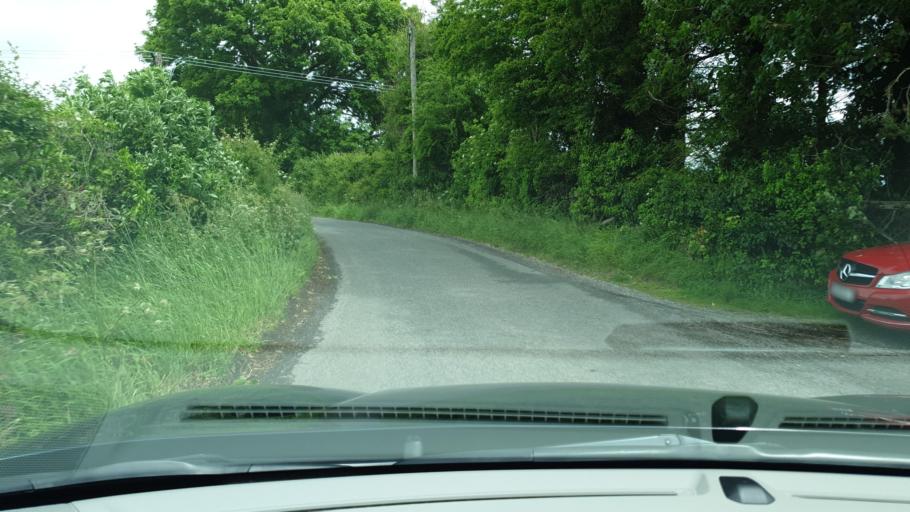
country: IE
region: Leinster
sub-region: Kildare
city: Leixlip
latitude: 53.3725
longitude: -6.5303
